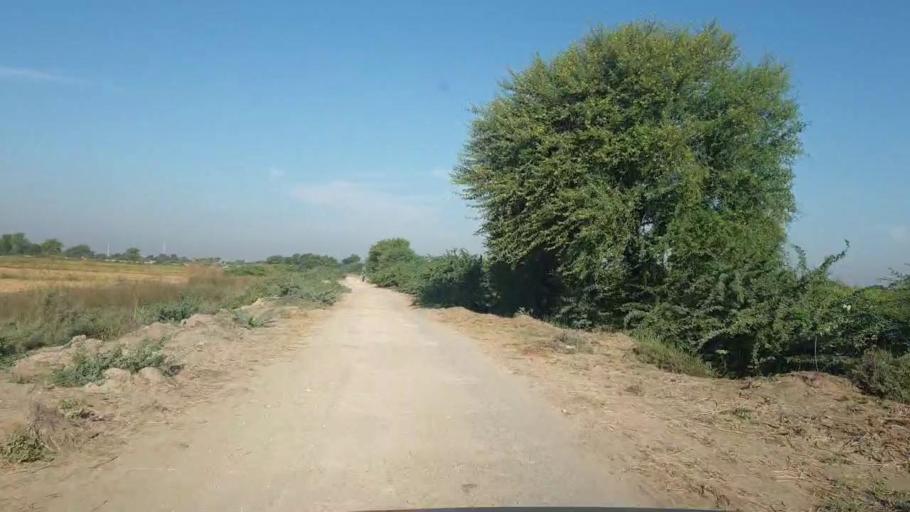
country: PK
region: Sindh
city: Talhar
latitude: 24.8256
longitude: 68.8212
